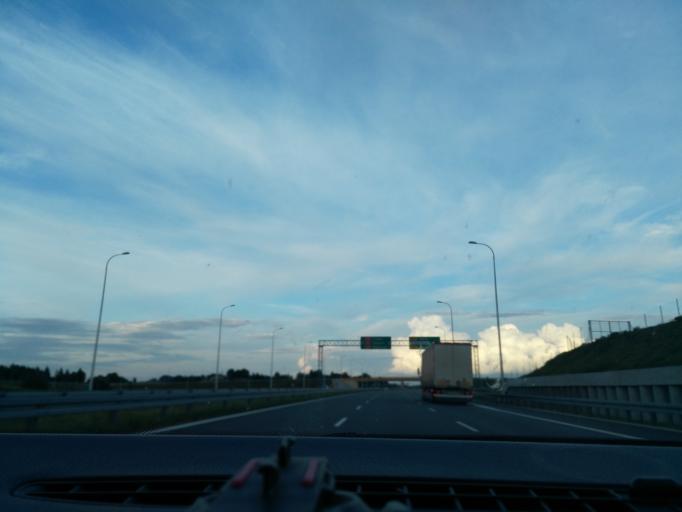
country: PL
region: Lublin Voivodeship
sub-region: Powiat lubelski
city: Lublin
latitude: 51.3011
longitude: 22.5110
